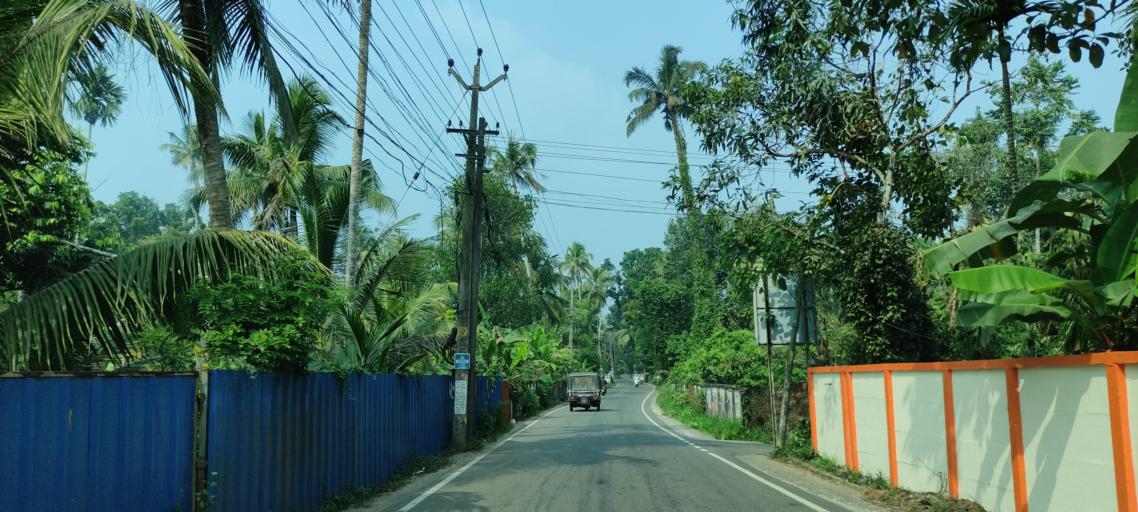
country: IN
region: Kerala
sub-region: Kottayam
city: Vaikam
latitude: 9.7417
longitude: 76.4012
